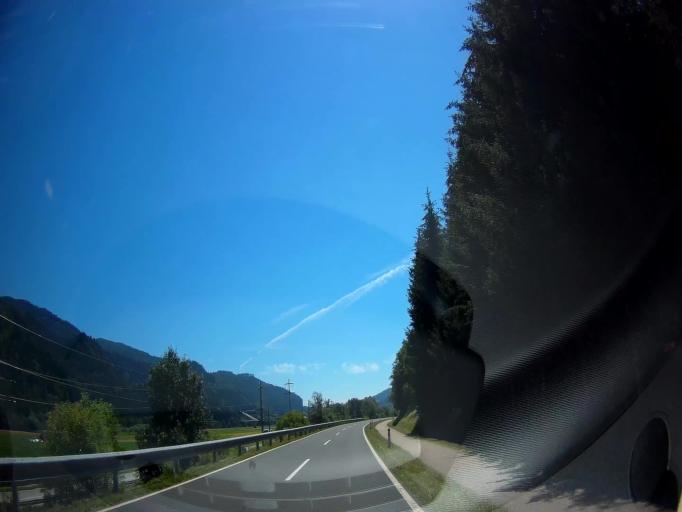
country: AT
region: Carinthia
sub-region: Politischer Bezirk Sankt Veit an der Glan
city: Micheldorf
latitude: 46.9286
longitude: 14.4268
